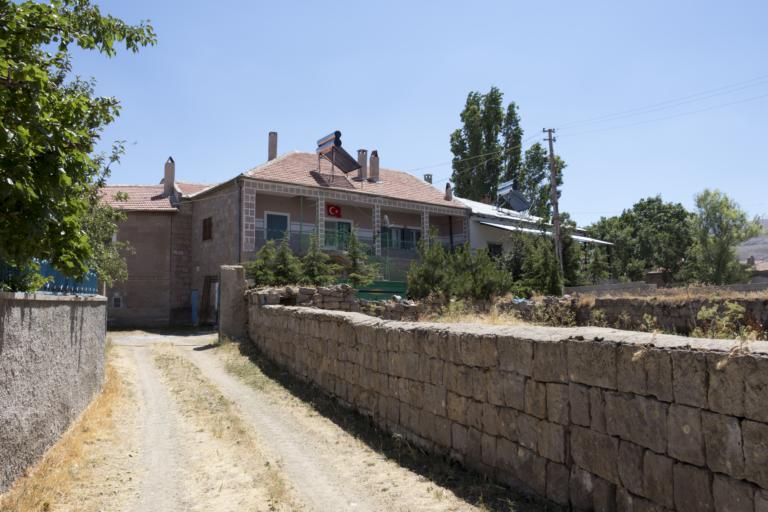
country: TR
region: Kayseri
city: Toklar
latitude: 38.4062
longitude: 36.0821
